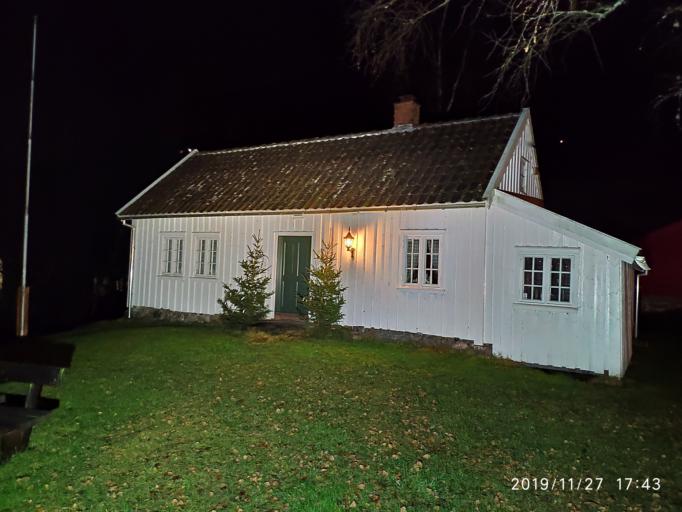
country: NO
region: Rogaland
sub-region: Lund
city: Moi
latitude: 58.4480
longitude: 6.5509
